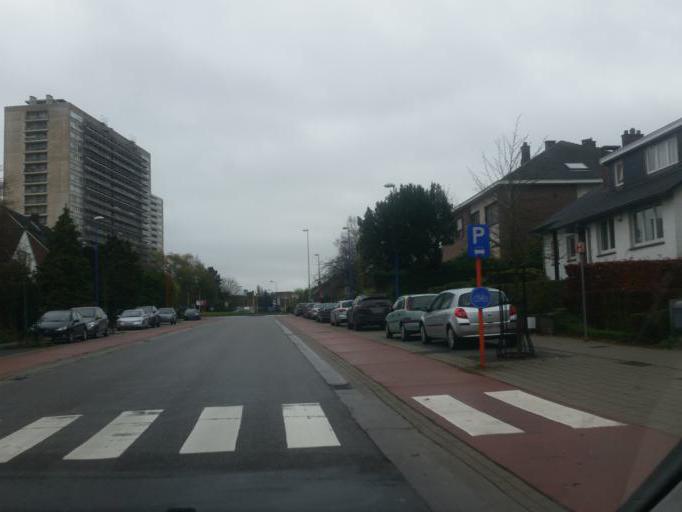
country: BE
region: Flanders
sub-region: Provincie Vlaams-Brabant
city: Grimbergen
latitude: 50.9029
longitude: 4.3573
